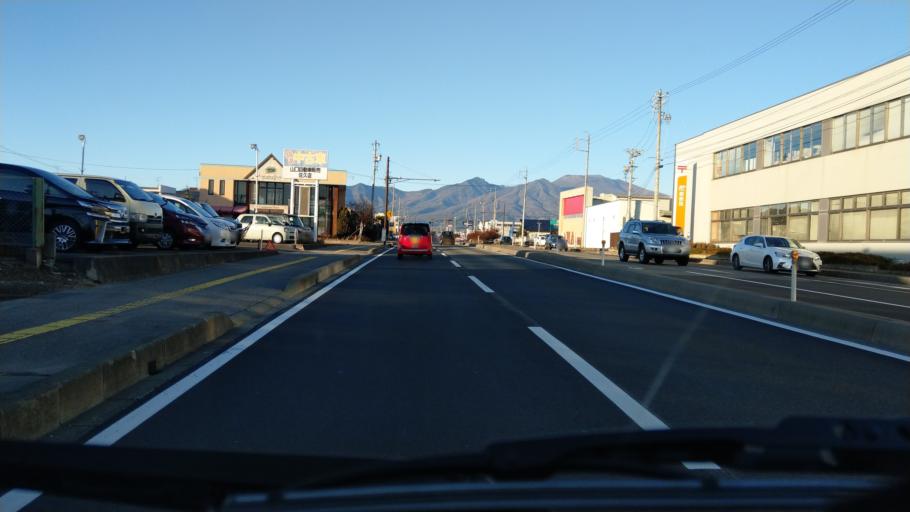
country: JP
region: Nagano
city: Saku
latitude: 36.2498
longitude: 138.4675
